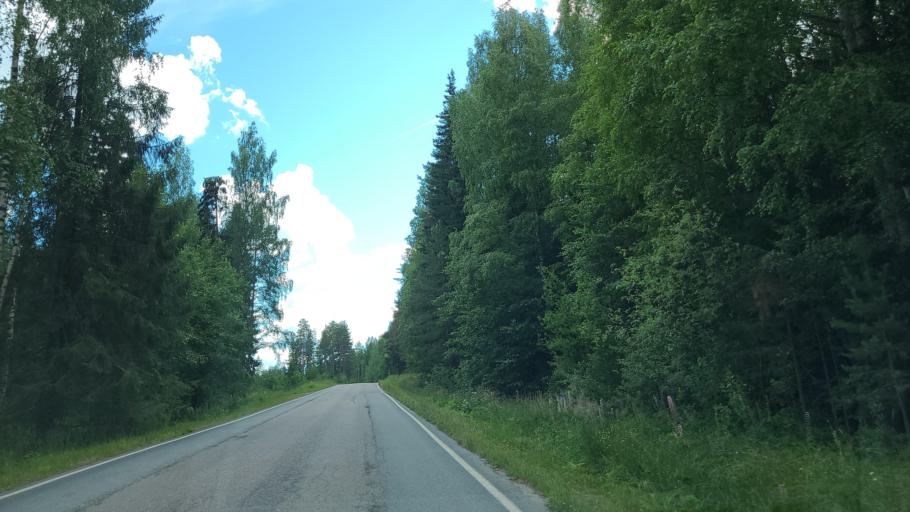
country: FI
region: Central Finland
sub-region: Jaemsae
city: Jaemsae
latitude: 61.8906
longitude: 25.2521
